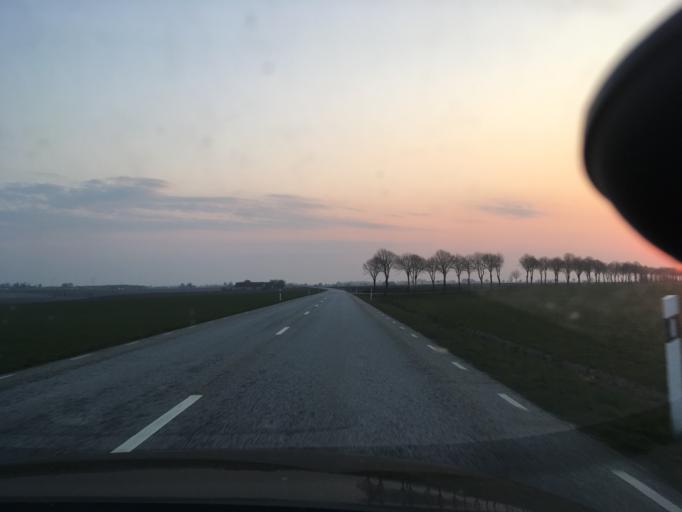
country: SE
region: Skane
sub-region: Ystads Kommun
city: Kopingebro
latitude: 55.4696
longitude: 14.0450
